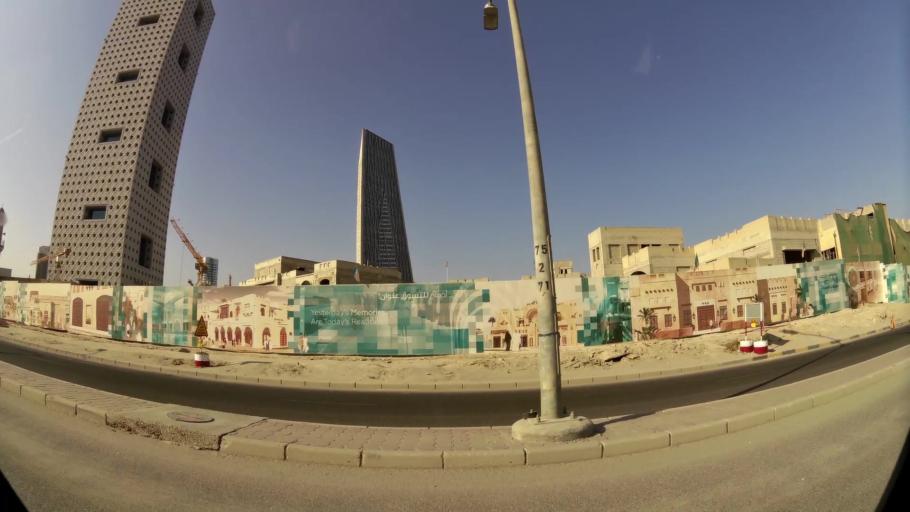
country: KW
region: Al Asimah
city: Kuwait City
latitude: 29.3845
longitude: 47.9807
